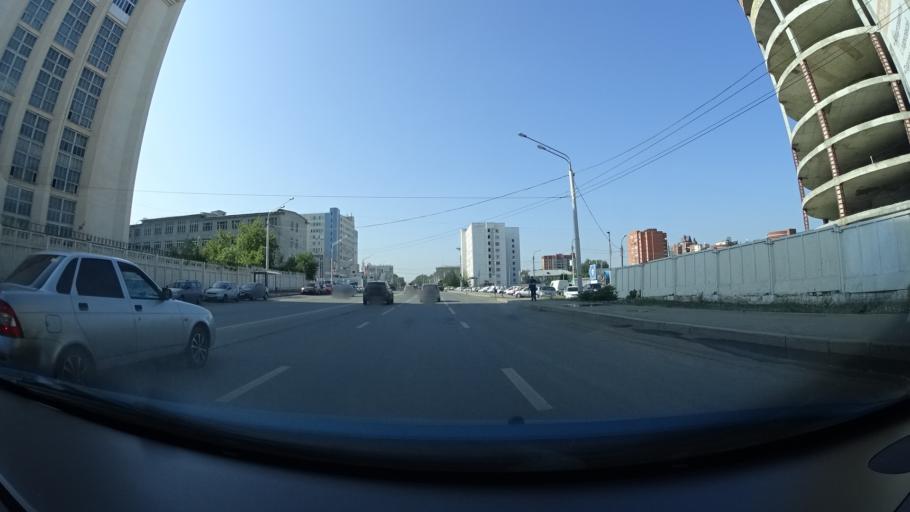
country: RU
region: Bashkortostan
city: Ufa
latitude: 54.7436
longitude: 55.9683
